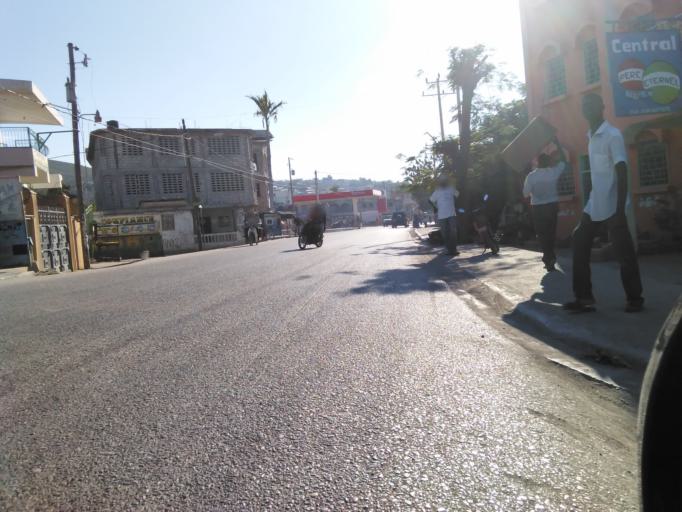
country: HT
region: Artibonite
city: Saint-Marc
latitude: 19.0987
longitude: -72.7032
